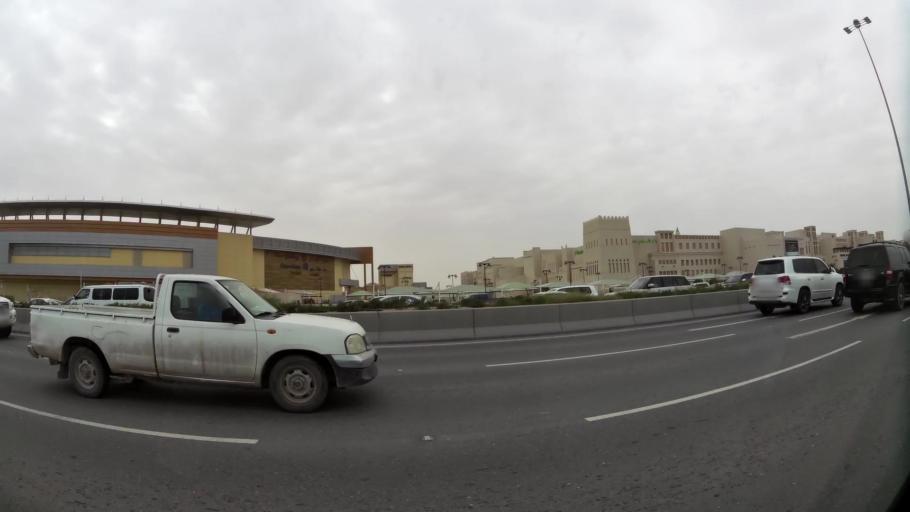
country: QA
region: Baladiyat ar Rayyan
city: Ar Rayyan
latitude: 25.3349
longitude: 51.4630
